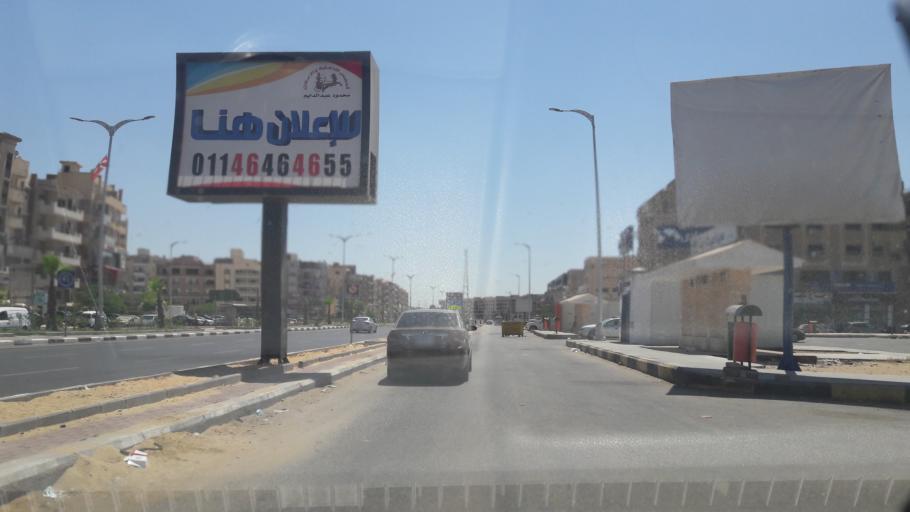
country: EG
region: Al Jizah
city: Madinat Sittah Uktubar
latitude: 29.9685
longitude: 30.9379
